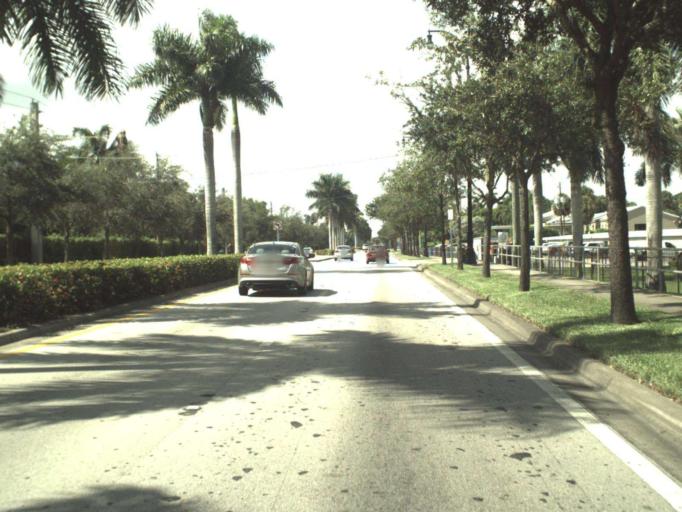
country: US
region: Florida
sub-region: Miami-Dade County
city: Biscayne Park
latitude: 25.8696
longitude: -80.1747
